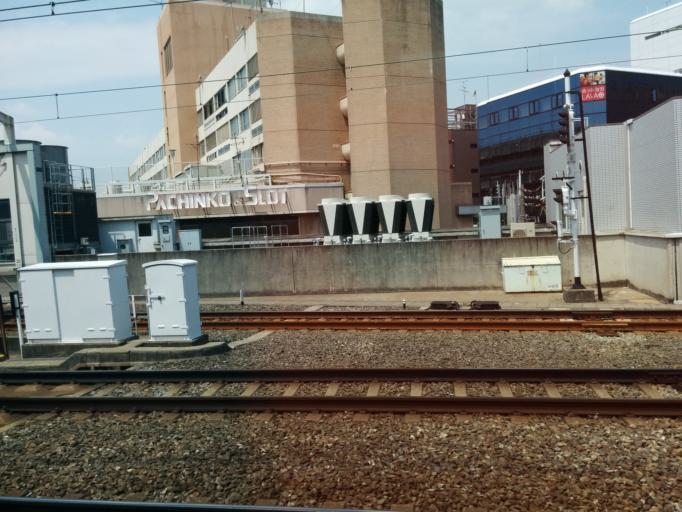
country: JP
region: Osaka
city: Ibaraki
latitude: 34.8174
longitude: 135.5764
